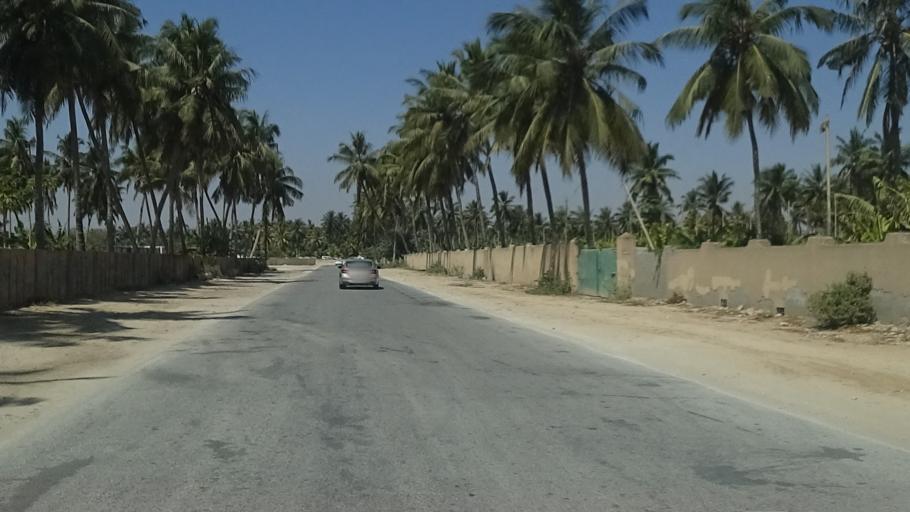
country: OM
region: Zufar
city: Salalah
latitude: 17.0220
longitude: 54.1234
